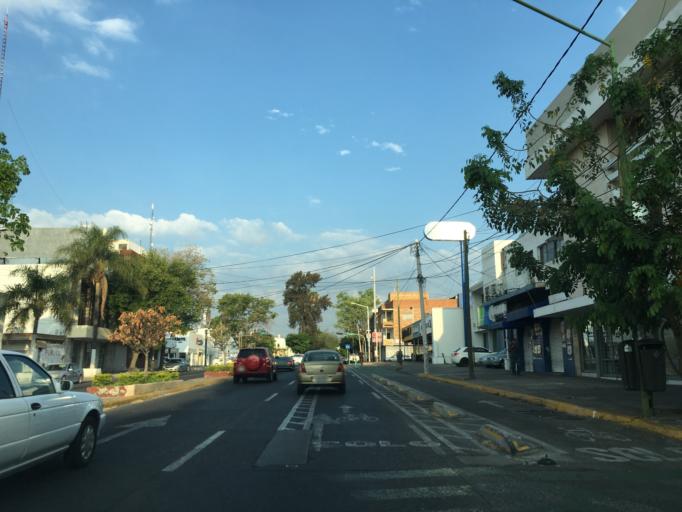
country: MX
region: Jalisco
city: Guadalajara
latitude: 20.6703
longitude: -103.3585
